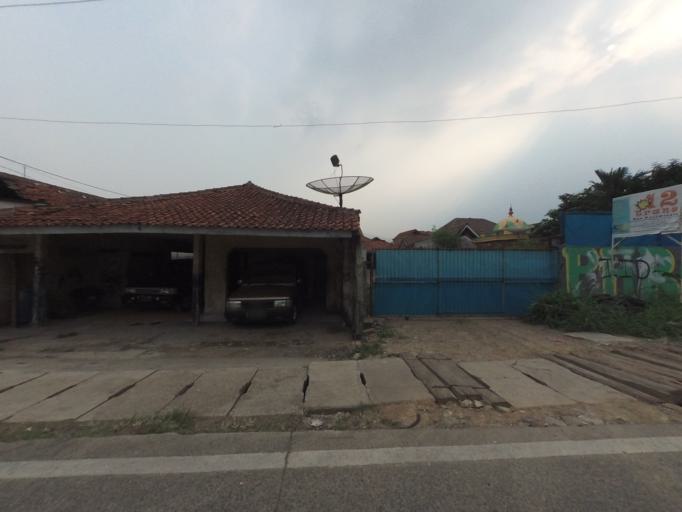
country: ID
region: West Java
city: Sidoger Lebak
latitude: -6.5651
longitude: 106.5914
